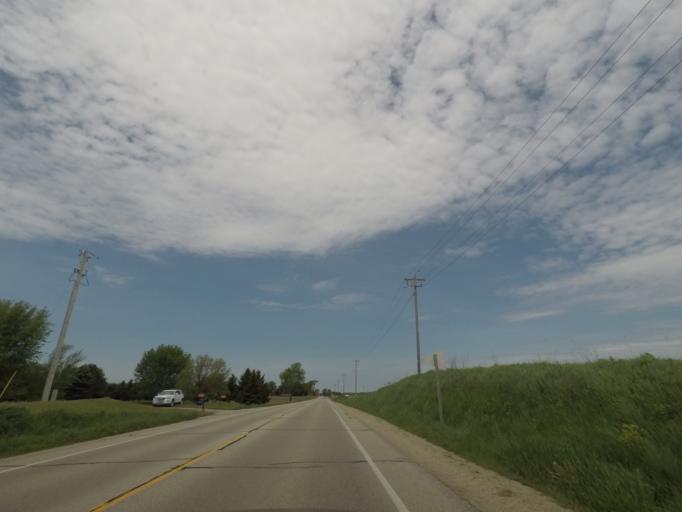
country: US
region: Wisconsin
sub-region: Green County
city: Brooklyn
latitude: 42.8364
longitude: -89.3211
